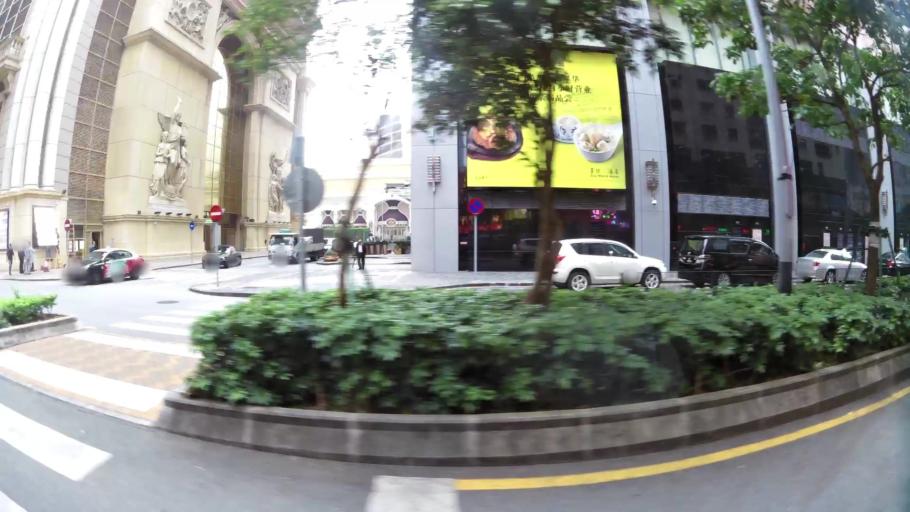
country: MO
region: Macau
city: Macau
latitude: 22.1899
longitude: 113.5486
